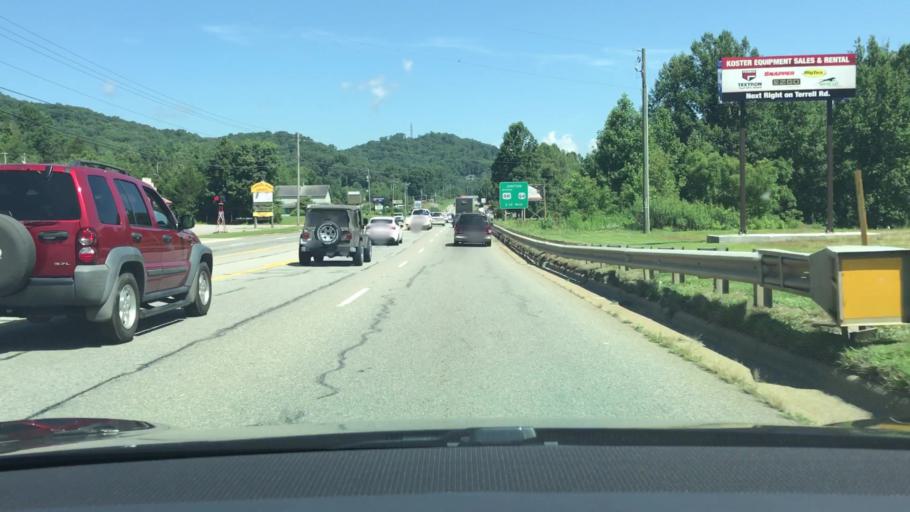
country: US
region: North Carolina
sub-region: Macon County
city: Franklin
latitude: 35.1293
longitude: -83.3957
